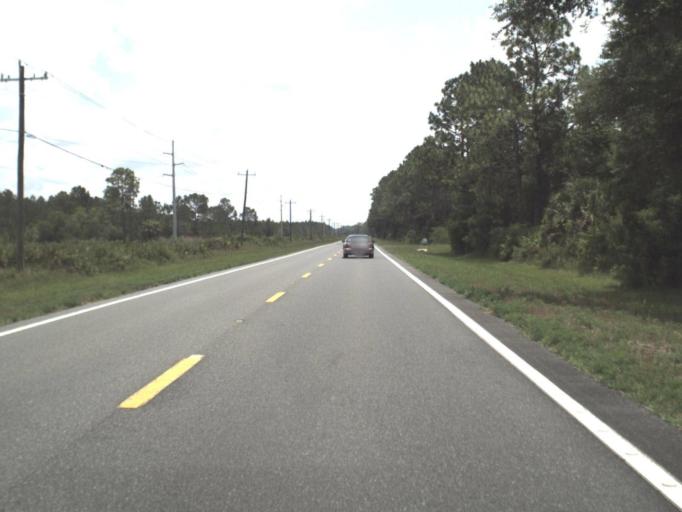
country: US
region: Florida
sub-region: Levy County
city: Chiefland
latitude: 29.2437
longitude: -82.9214
